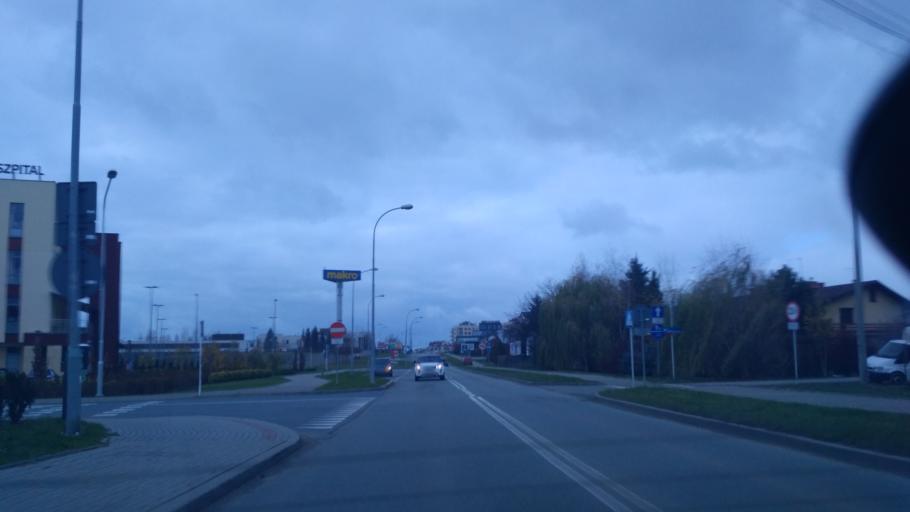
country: PL
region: Subcarpathian Voivodeship
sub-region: Rzeszow
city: Rzeszow
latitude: 50.0318
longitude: 22.0405
